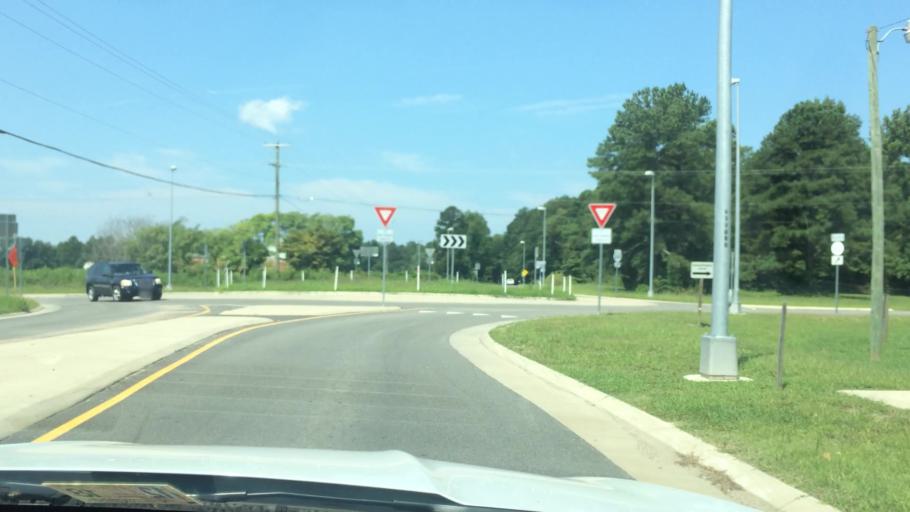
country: US
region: Virginia
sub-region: New Kent County
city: New Kent
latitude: 37.5327
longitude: -77.1148
